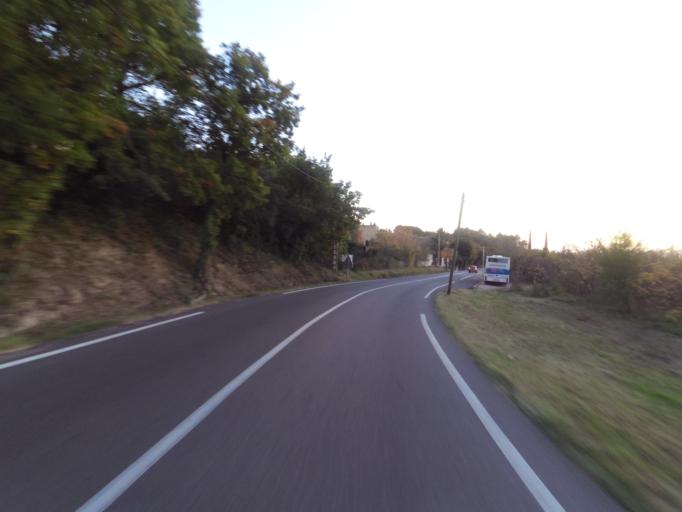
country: FR
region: Provence-Alpes-Cote d'Azur
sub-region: Departement du Vaucluse
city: Caromb
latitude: 44.1024
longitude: 5.1458
